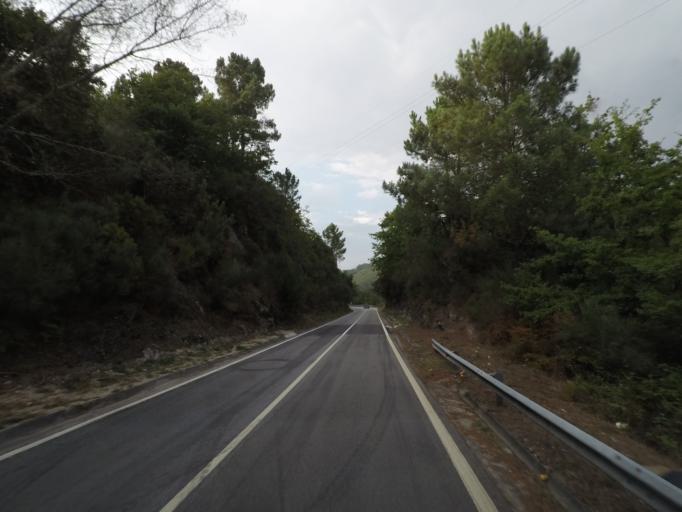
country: PT
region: Porto
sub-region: Baiao
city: Valadares
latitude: 41.2181
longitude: -7.9888
